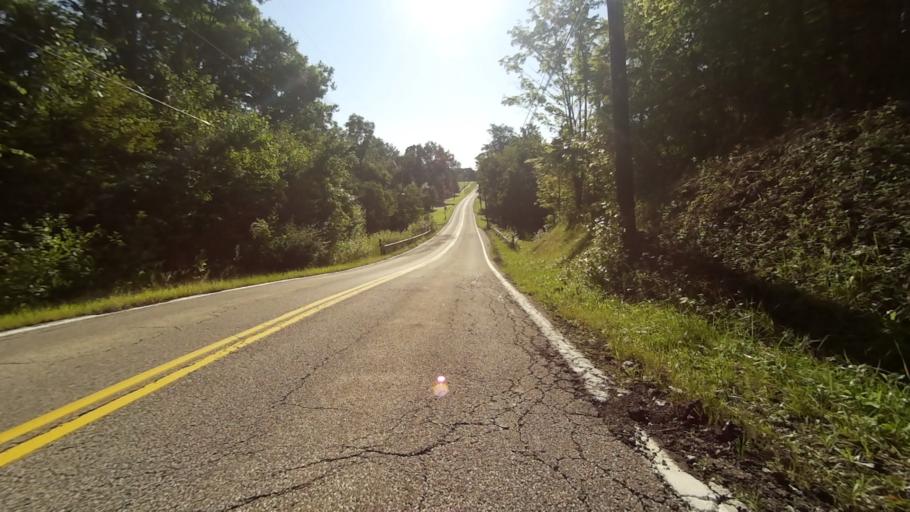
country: US
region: Ohio
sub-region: Portage County
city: Aurora
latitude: 41.3042
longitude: -81.3115
